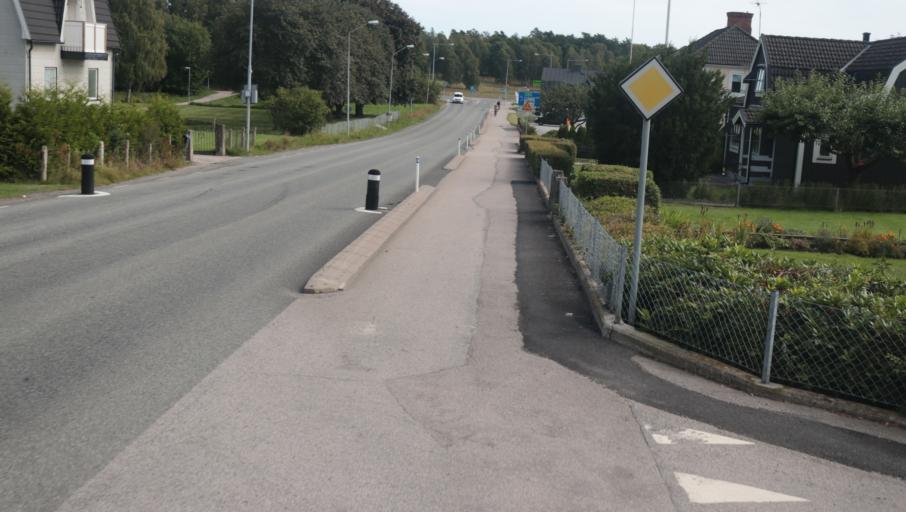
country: SE
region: Blekinge
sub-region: Karlshamns Kommun
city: Karlshamn
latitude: 56.2001
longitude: 14.8326
